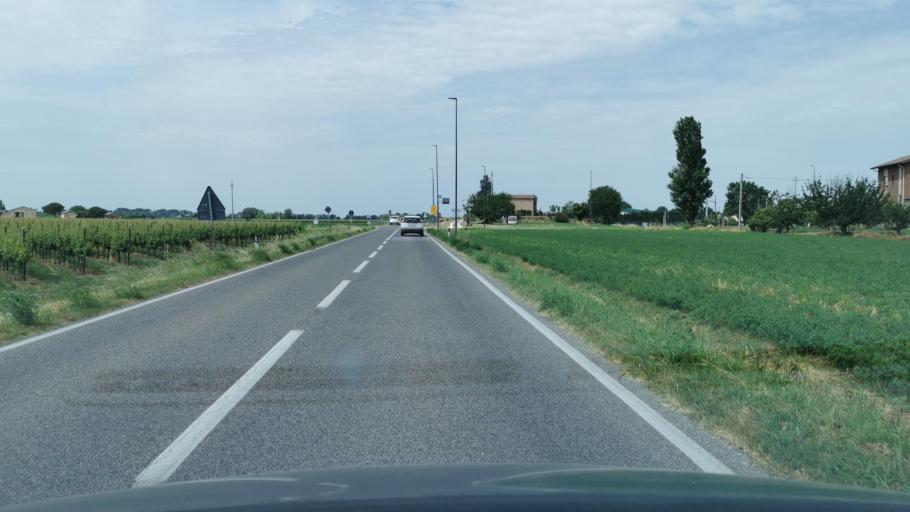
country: IT
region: Emilia-Romagna
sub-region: Provincia di Ravenna
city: Savarna-Conventella
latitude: 44.5081
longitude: 12.1003
